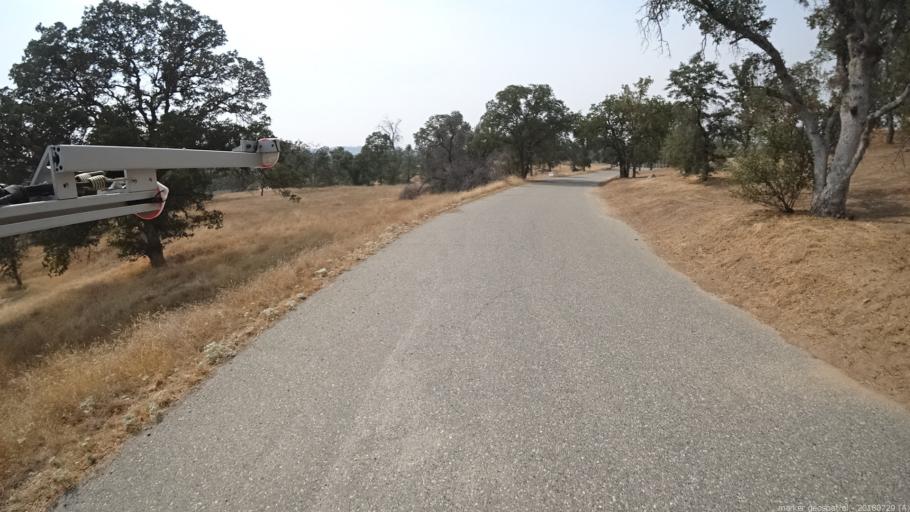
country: US
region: California
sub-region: Madera County
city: Yosemite Lakes
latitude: 37.2357
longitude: -119.7703
